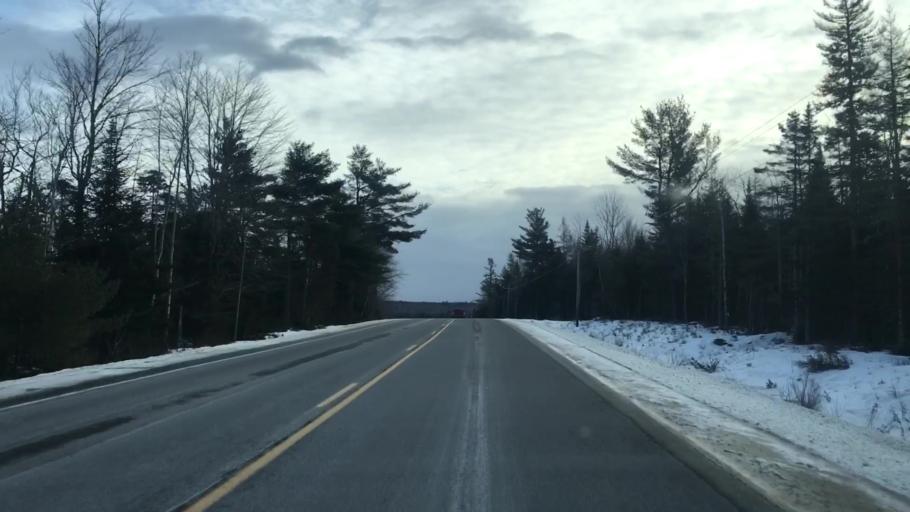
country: US
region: Maine
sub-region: Washington County
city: Machias
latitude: 44.9995
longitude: -67.5937
